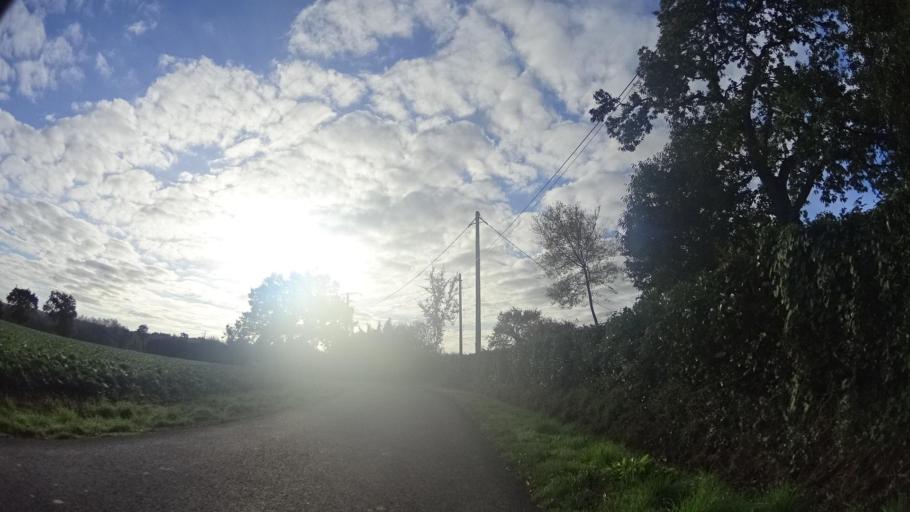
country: FR
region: Brittany
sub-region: Departement des Cotes-d'Armor
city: Evran
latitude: 48.3558
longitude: -1.9450
